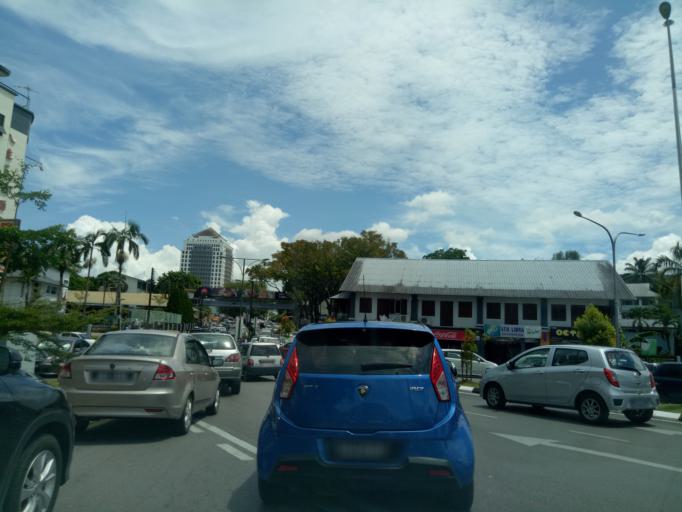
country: MY
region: Sarawak
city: Kuching
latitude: 1.5552
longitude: 110.3476
